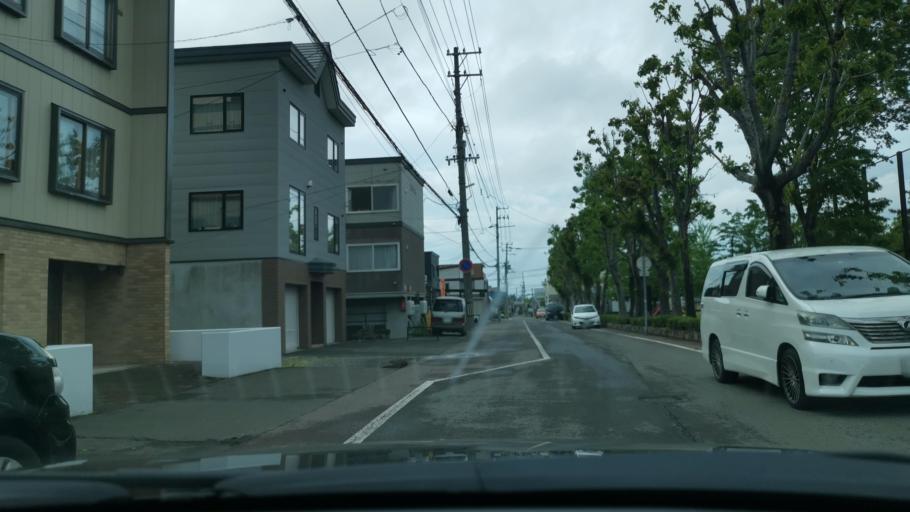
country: JP
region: Hokkaido
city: Sapporo
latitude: 43.0845
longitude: 141.2964
